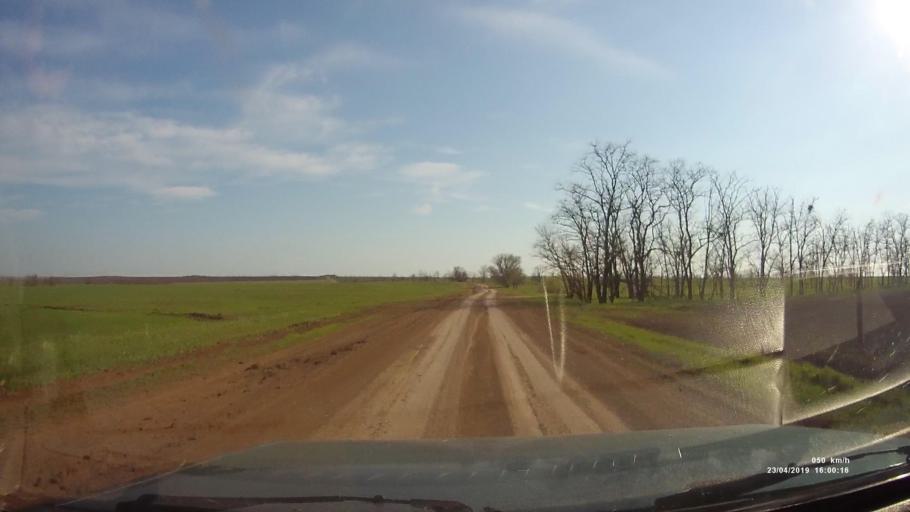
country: RU
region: Rostov
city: Remontnoye
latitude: 46.5105
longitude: 43.1080
